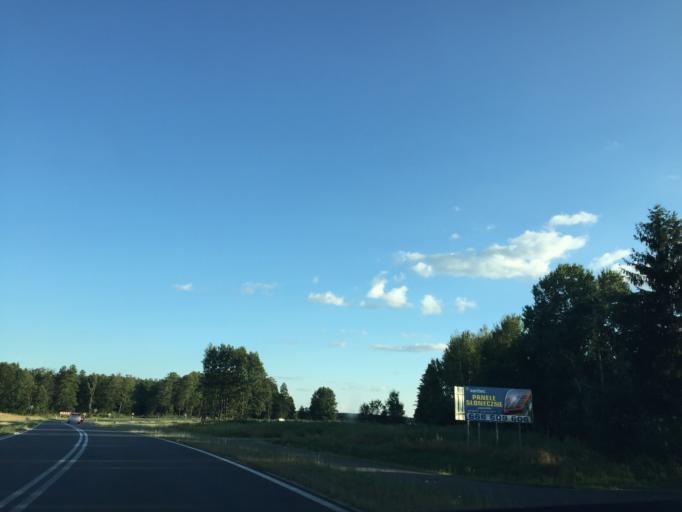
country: PL
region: Podlasie
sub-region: Lomza
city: Lomza
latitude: 53.1279
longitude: 22.0482
